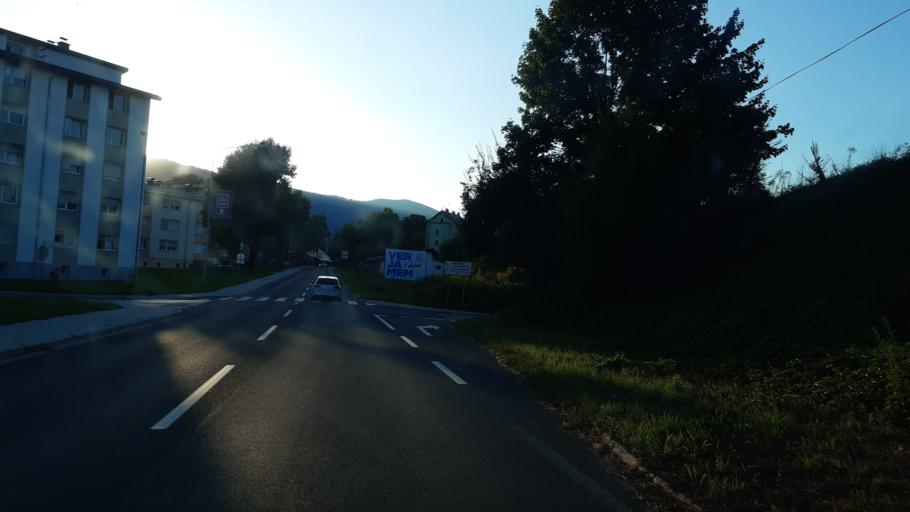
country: SI
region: Kocevje
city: Kocevje
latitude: 45.6431
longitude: 14.8608
